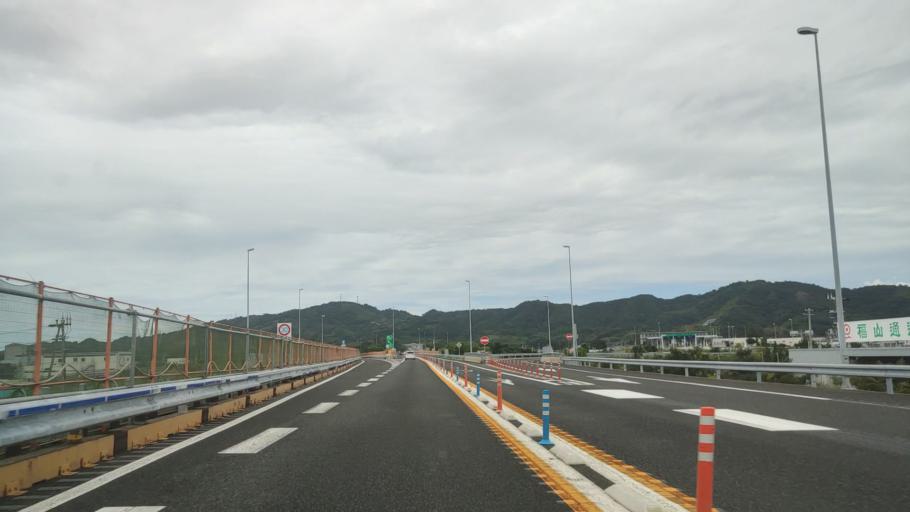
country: JP
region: Wakayama
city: Tanabe
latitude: 33.7772
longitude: 135.3292
